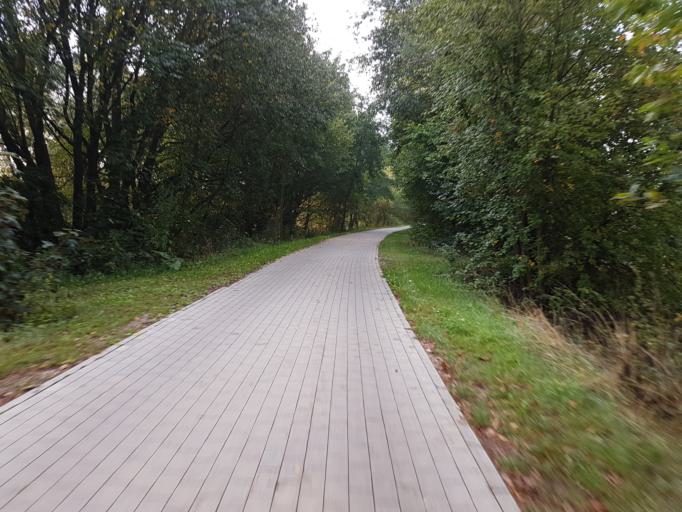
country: DE
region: Saxony
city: Wittgensdorf
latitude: 50.8865
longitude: 12.8915
